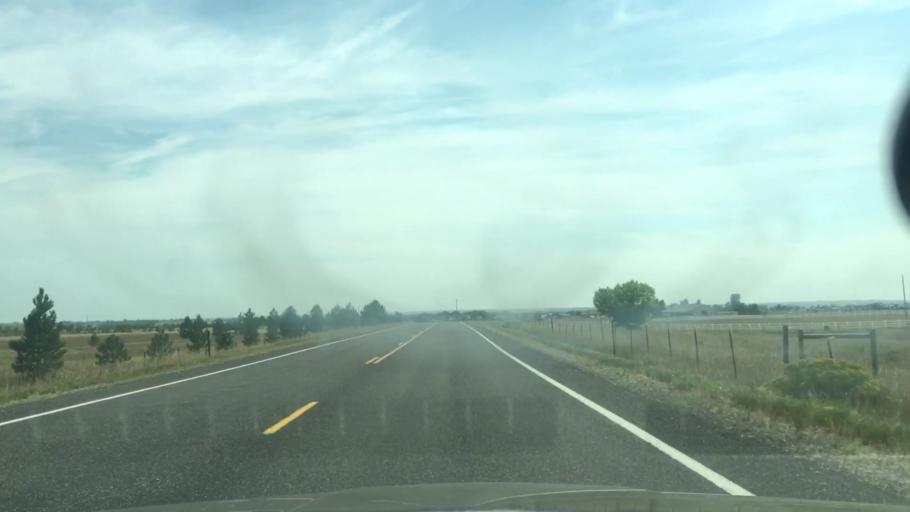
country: US
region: Colorado
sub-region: Larimer County
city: Berthoud
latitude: 40.3353
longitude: -105.1675
